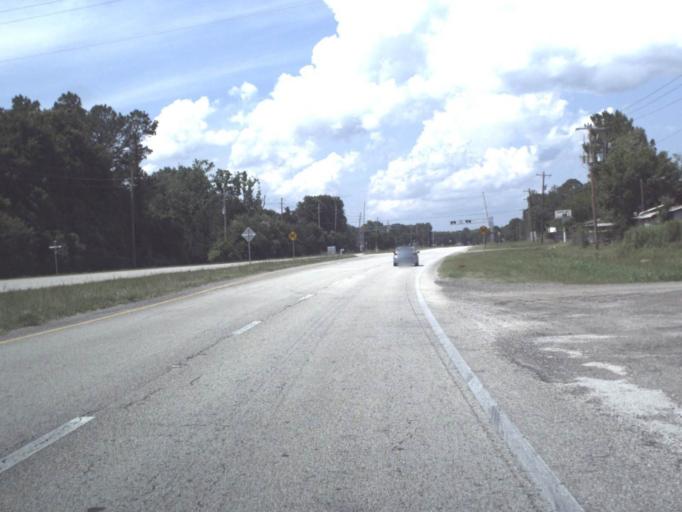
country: US
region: Florida
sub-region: Clay County
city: Green Cove Springs
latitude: 29.9728
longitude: -81.6762
